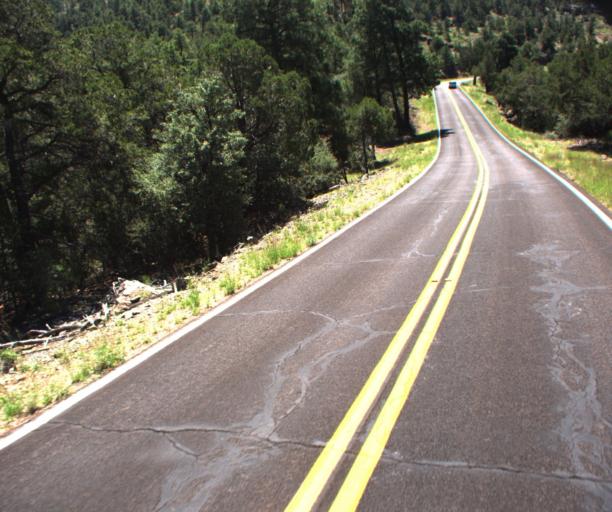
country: US
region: Arizona
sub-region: Greenlee County
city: Morenci
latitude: 33.4060
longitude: -109.3489
